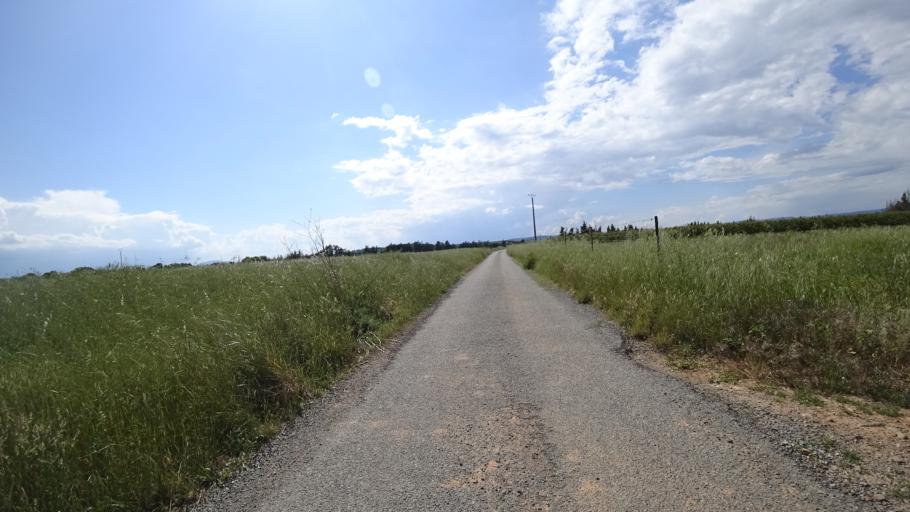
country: FR
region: Languedoc-Roussillon
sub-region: Departement de l'Aude
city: Ginestas
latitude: 43.2639
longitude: 2.8998
